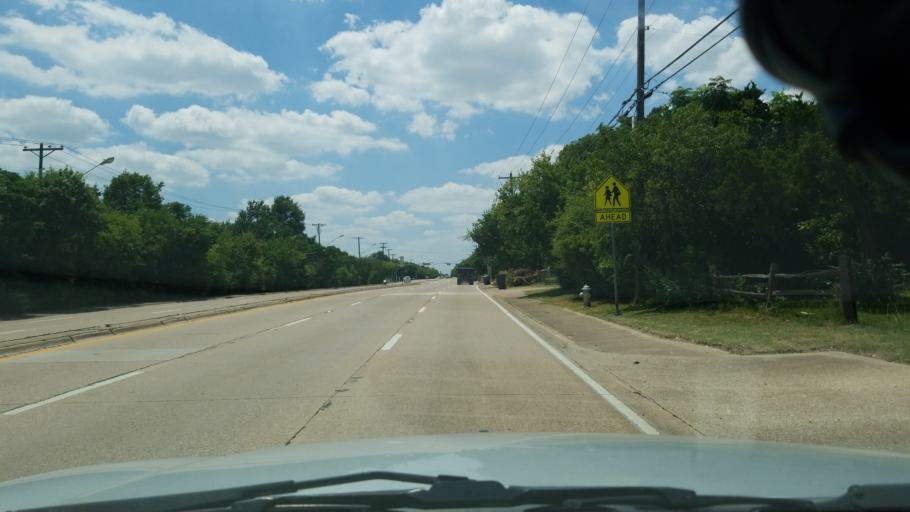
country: US
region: Texas
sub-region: Dallas County
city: Cockrell Hill
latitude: 32.6914
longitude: -96.8713
